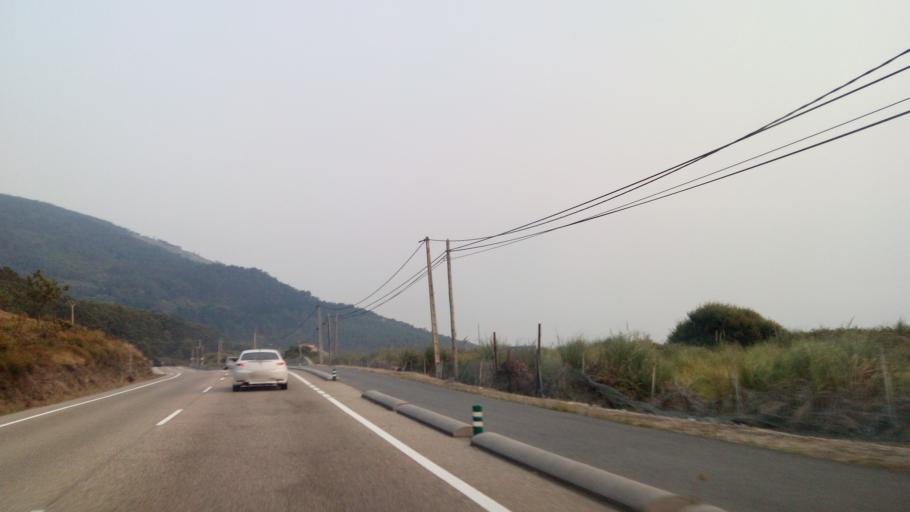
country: ES
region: Galicia
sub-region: Provincia de Pontevedra
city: Baiona
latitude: 42.0904
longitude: -8.8927
